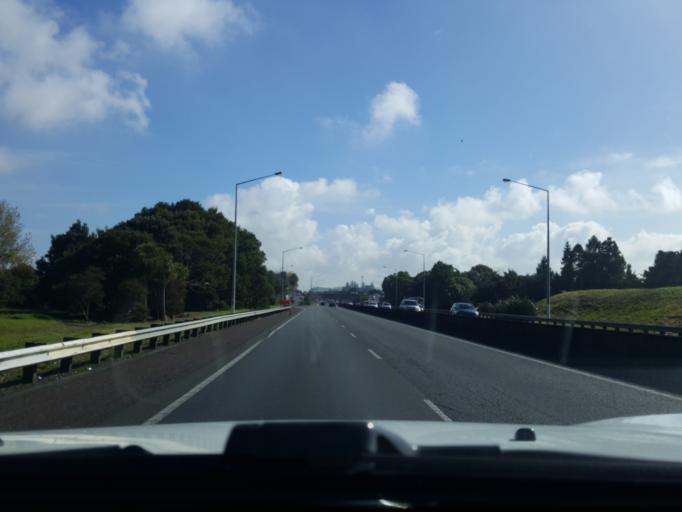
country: NZ
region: Auckland
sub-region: Auckland
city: Mangere
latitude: -36.9763
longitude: 174.8216
